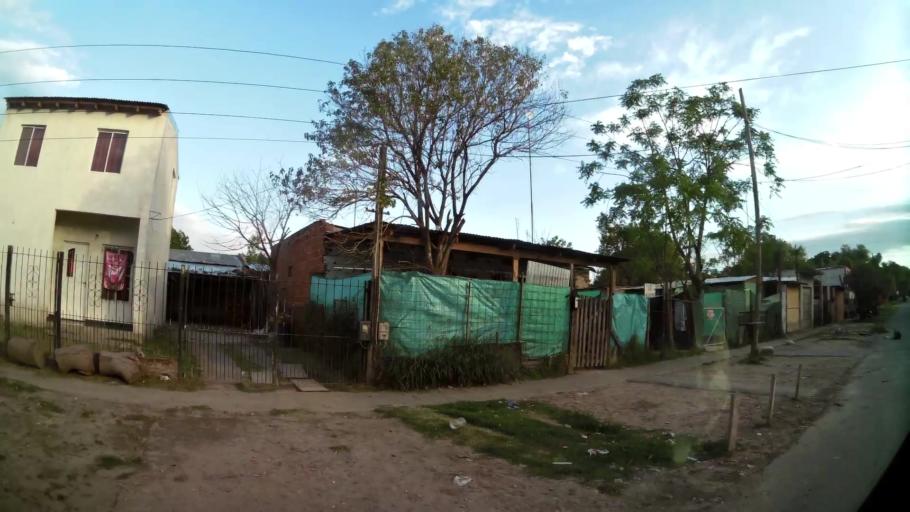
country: AR
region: Buenos Aires
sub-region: Partido de Tigre
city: Tigre
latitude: -34.4486
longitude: -58.6546
